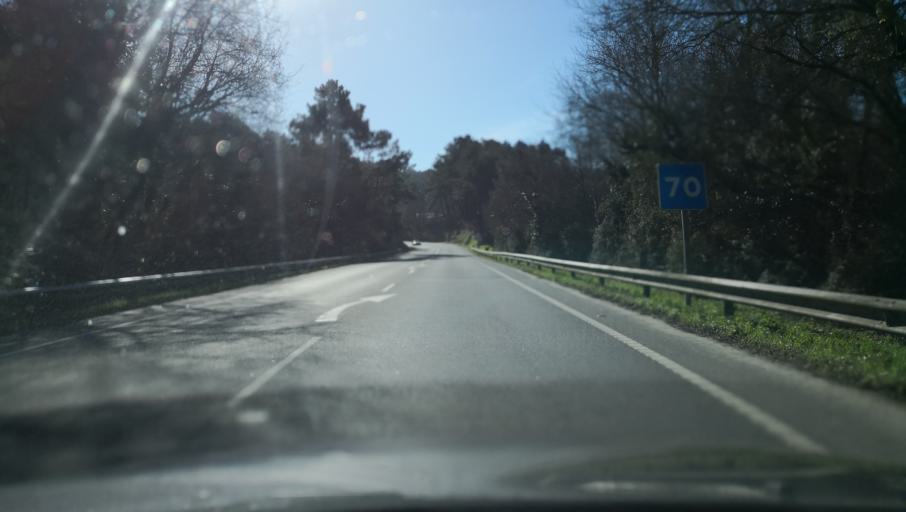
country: ES
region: Galicia
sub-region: Provincia de Pontevedra
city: Silleda
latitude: 42.7321
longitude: -8.3193
